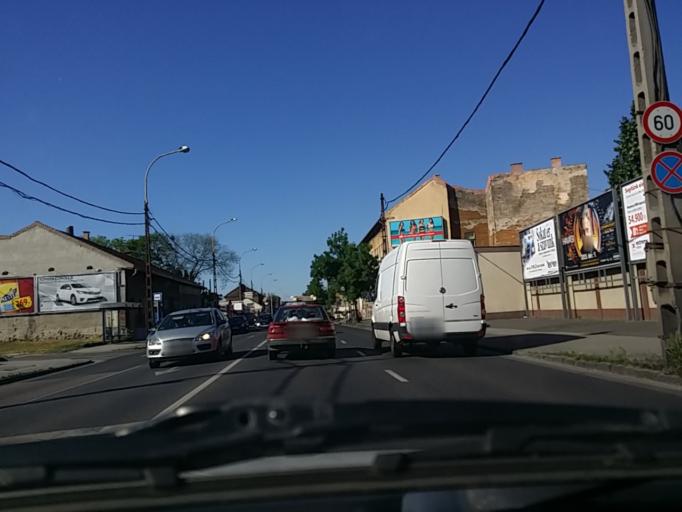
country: HU
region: Budapest
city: Budapest IV. keruelet
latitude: 47.5652
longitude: 19.0792
